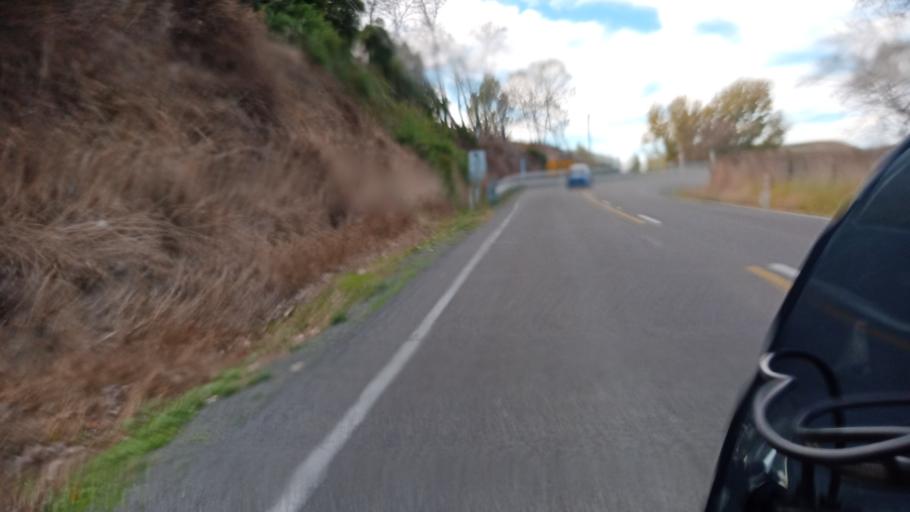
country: NZ
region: Gisborne
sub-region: Gisborne District
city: Gisborne
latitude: -38.8209
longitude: 177.9047
